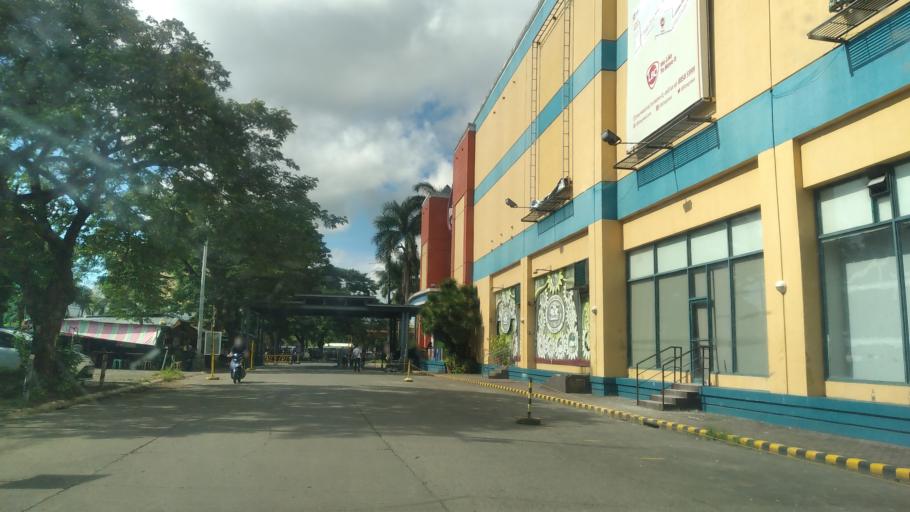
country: PH
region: Calabarzon
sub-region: Province of Quezon
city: Lucena
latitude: 13.9375
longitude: 121.6096
